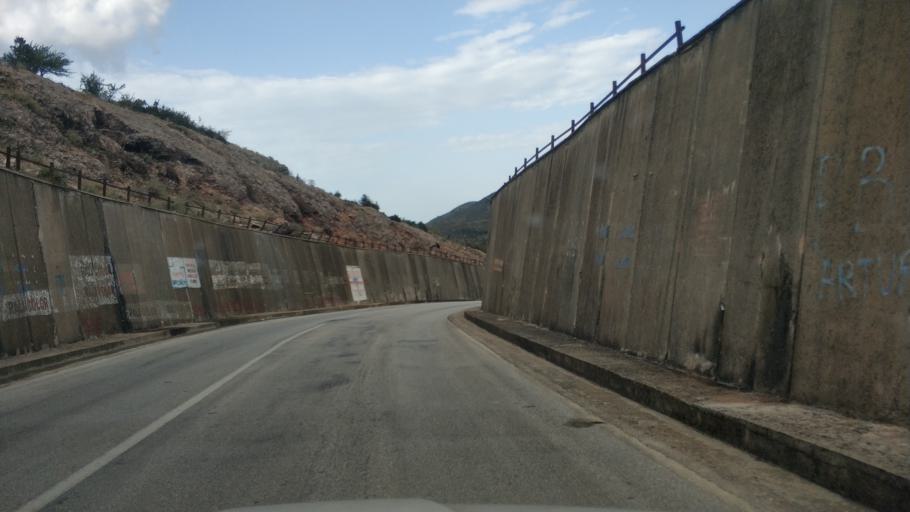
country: AL
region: Vlore
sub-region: Rrethi i Vlores
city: Orikum
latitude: 40.2650
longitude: 19.5161
